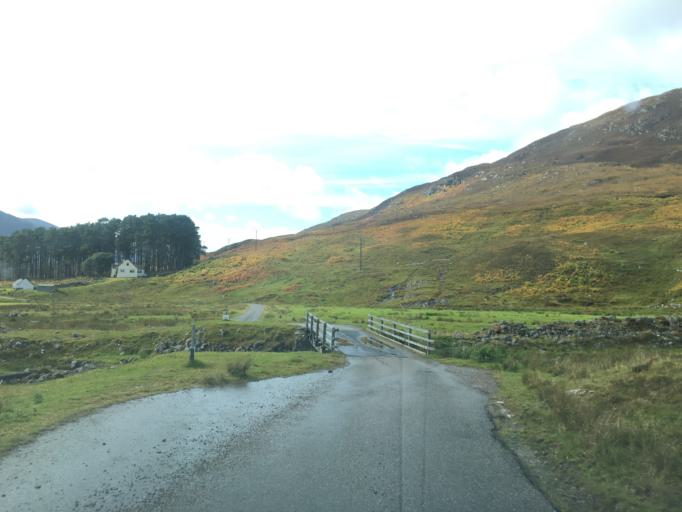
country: GB
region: Scotland
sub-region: Highland
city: Spean Bridge
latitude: 57.3512
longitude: -4.9073
